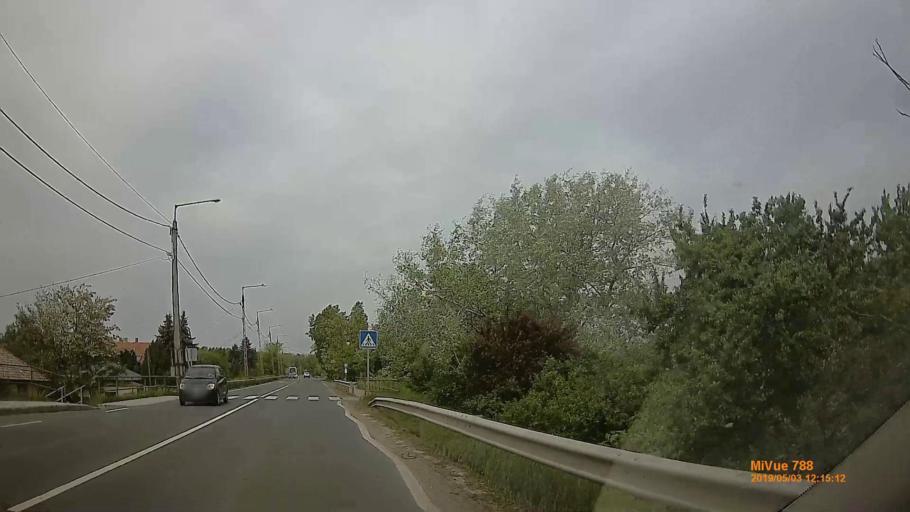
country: HU
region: Jasz-Nagykun-Szolnok
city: Szolnok
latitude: 47.1421
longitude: 20.2055
